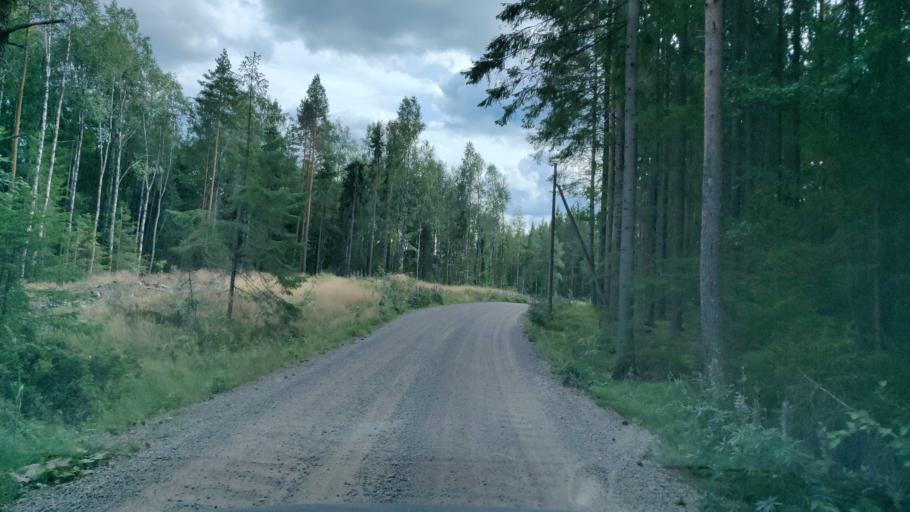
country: SE
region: Vaermland
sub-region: Hagfors Kommun
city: Hagfors
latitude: 60.0146
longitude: 13.7050
